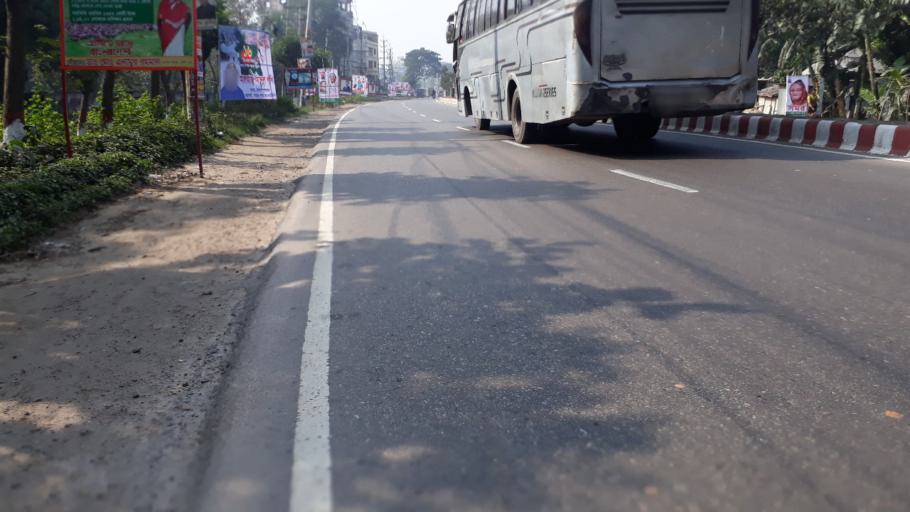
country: BD
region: Dhaka
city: Tungi
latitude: 23.8617
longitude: 90.2660
